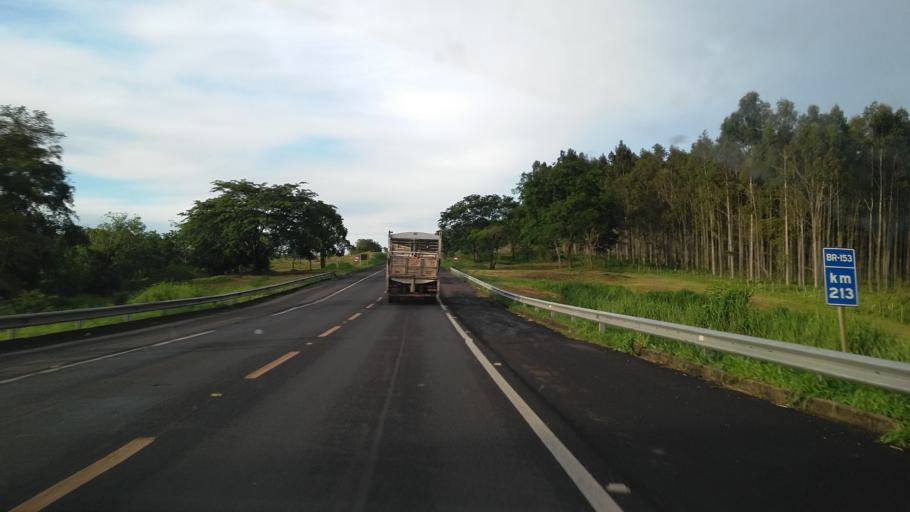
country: BR
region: Sao Paulo
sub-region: Marilia
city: Marilia
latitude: -21.9326
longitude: -49.9188
